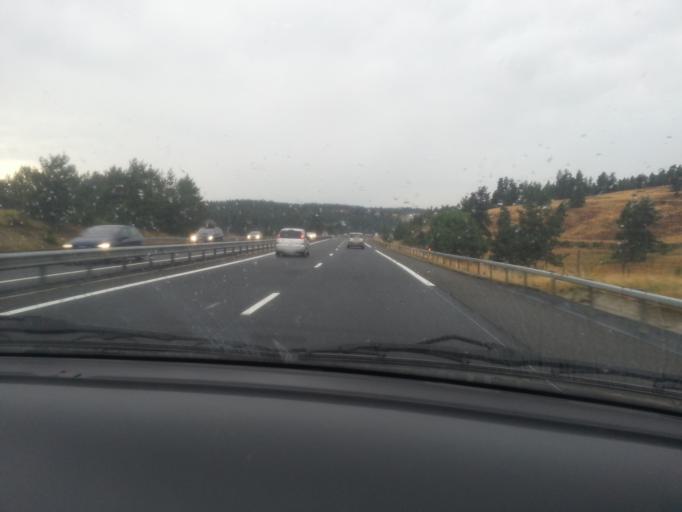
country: FR
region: Languedoc-Roussillon
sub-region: Departement de la Lozere
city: Aumont-Aubrac
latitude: 44.7007
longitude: 3.2816
